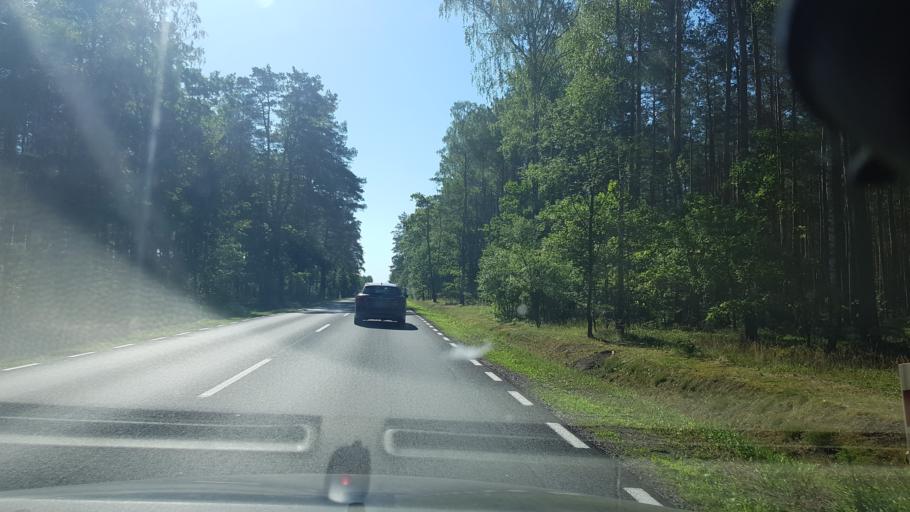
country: PL
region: Masovian Voivodeship
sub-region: Powiat wyszkowski
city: Branszczyk
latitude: 52.5661
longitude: 21.5551
